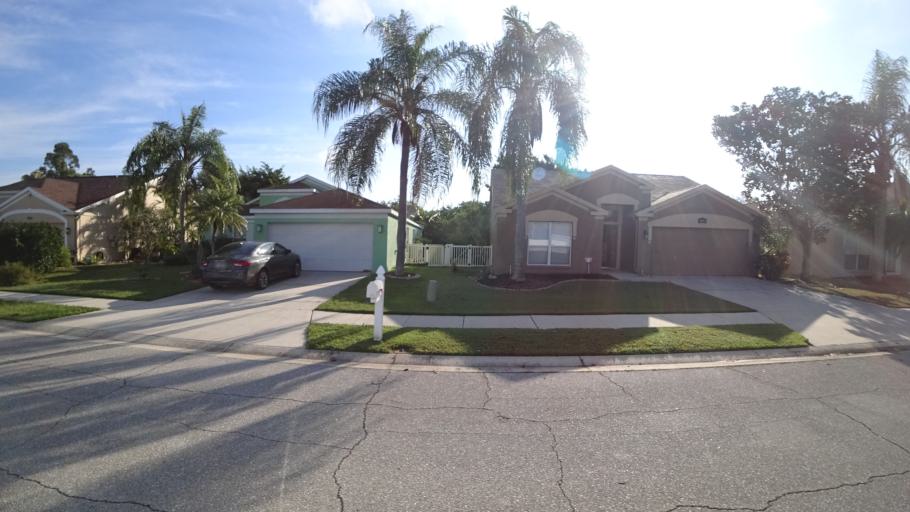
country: US
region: Florida
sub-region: Manatee County
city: Samoset
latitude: 27.4575
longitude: -82.5021
